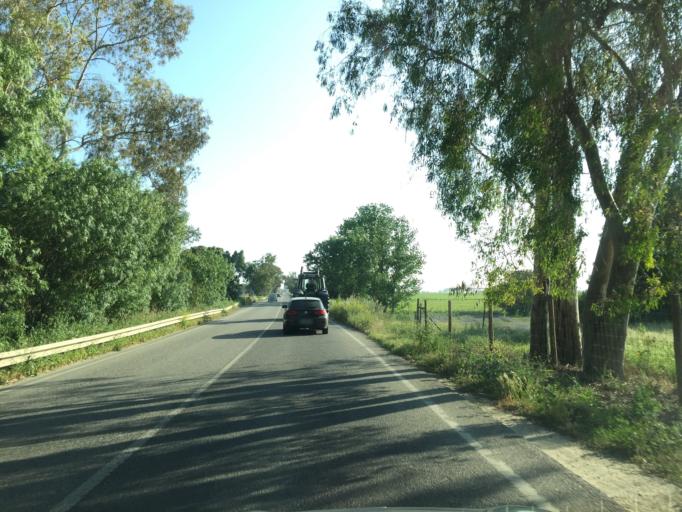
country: PT
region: Santarem
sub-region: Almeirim
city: Almeirim
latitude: 39.1988
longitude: -8.6407
